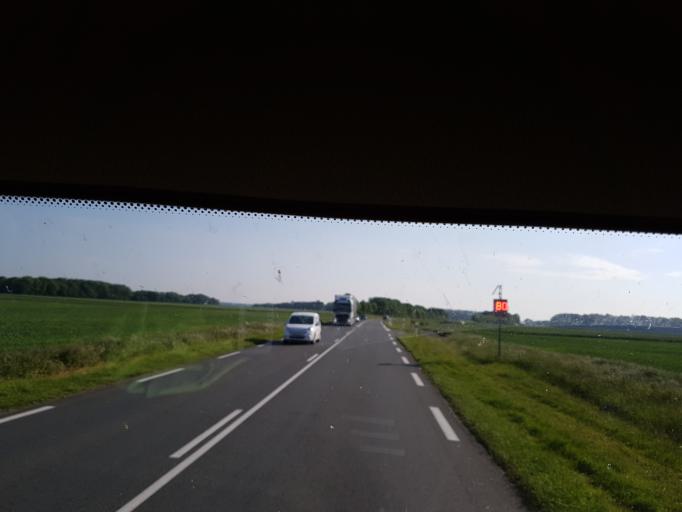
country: FR
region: Picardie
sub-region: Departement de la Somme
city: Crecy-en-Ponthieu
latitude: 50.1993
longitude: 1.8907
